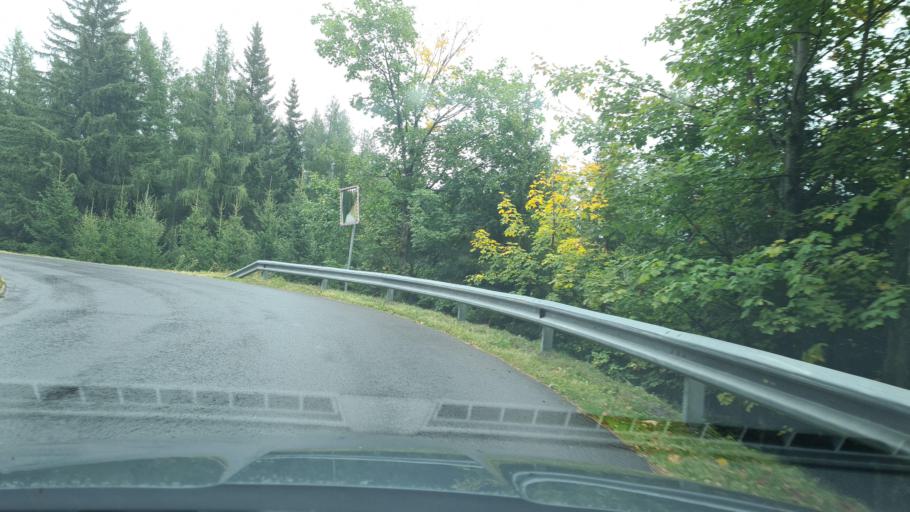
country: AT
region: Styria
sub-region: Politischer Bezirk Weiz
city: Passail
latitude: 47.3333
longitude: 15.4758
